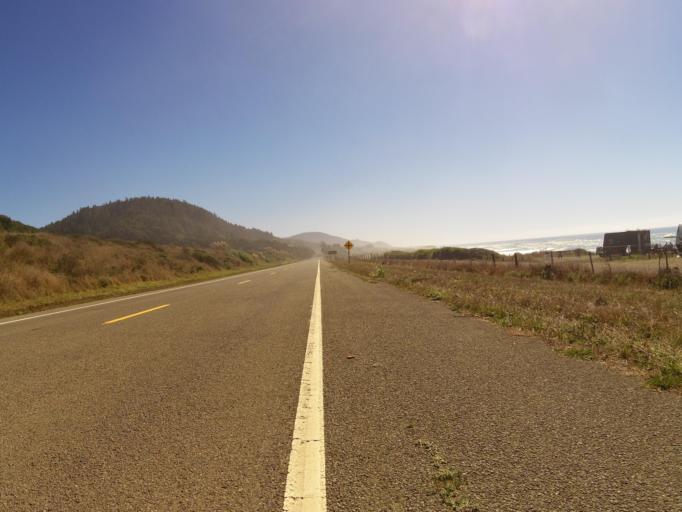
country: US
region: California
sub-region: Mendocino County
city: Fort Bragg
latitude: 39.6836
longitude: -123.7914
